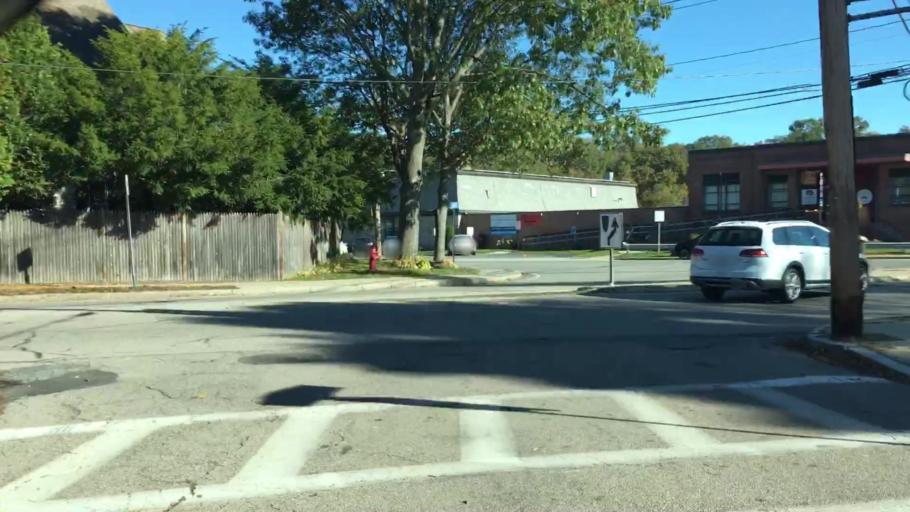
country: US
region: Massachusetts
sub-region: Middlesex County
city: Ashland
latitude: 42.2619
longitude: -71.4670
